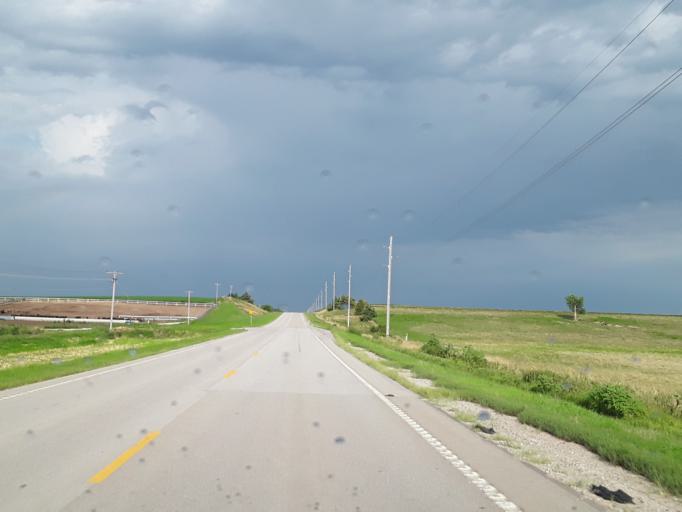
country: US
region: Nebraska
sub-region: Saunders County
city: Ashland
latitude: 41.0887
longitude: -96.4159
